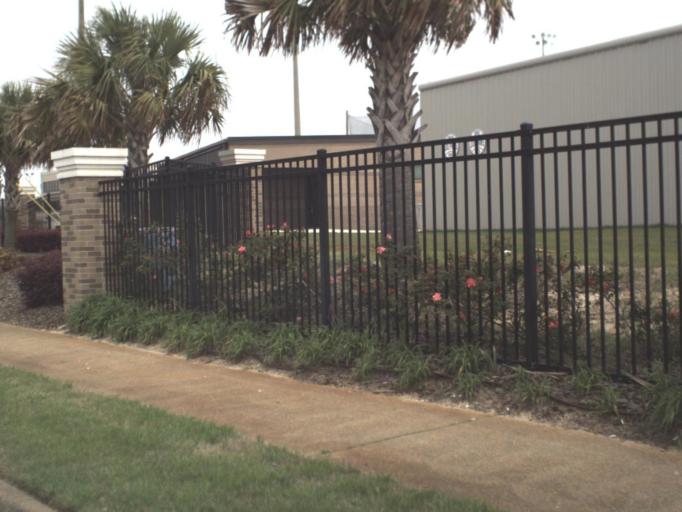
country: US
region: Florida
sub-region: Santa Rosa County
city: Gulf Breeze
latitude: 30.3629
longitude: -87.1688
